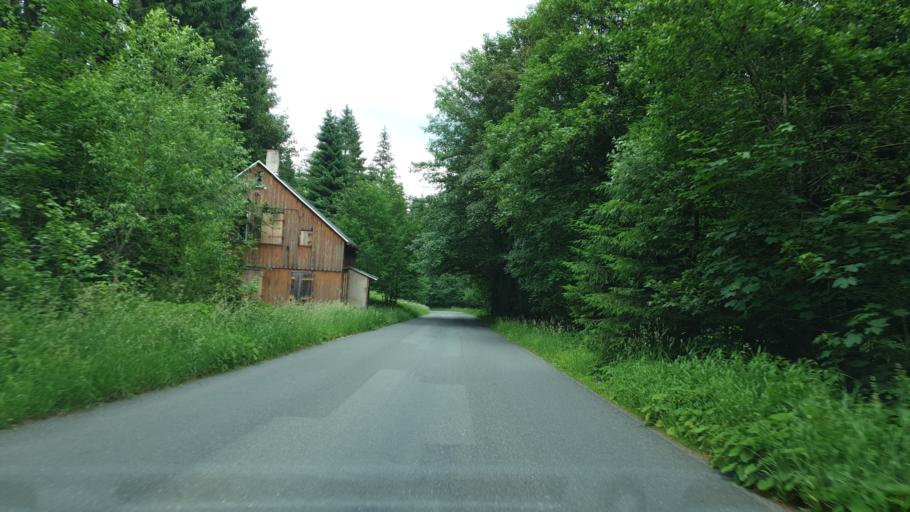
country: DE
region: Saxony
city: Tannenbergsthal
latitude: 50.4232
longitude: 12.4569
